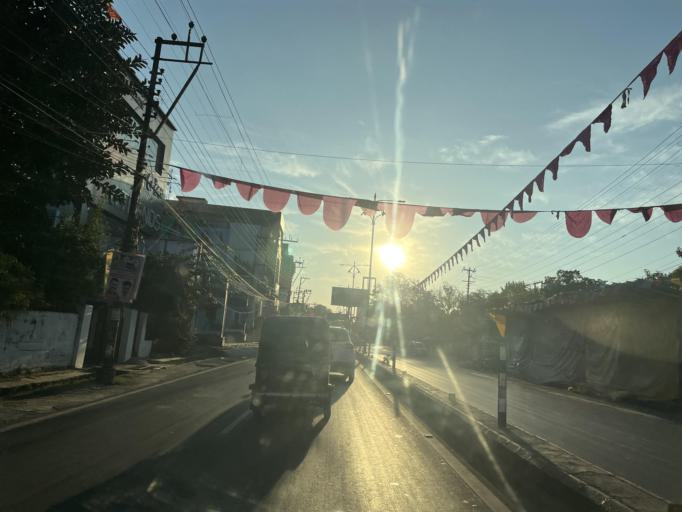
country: IN
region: Uttarakhand
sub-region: Naini Tal
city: Haldwani
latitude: 29.2167
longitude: 79.5225
